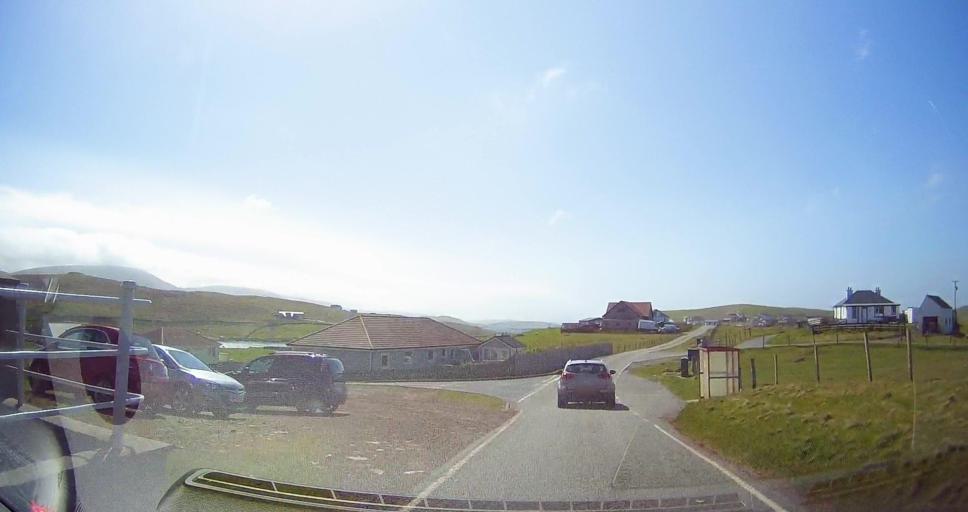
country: GB
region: Scotland
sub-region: Shetland Islands
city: Sandwick
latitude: 60.0867
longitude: -1.3307
